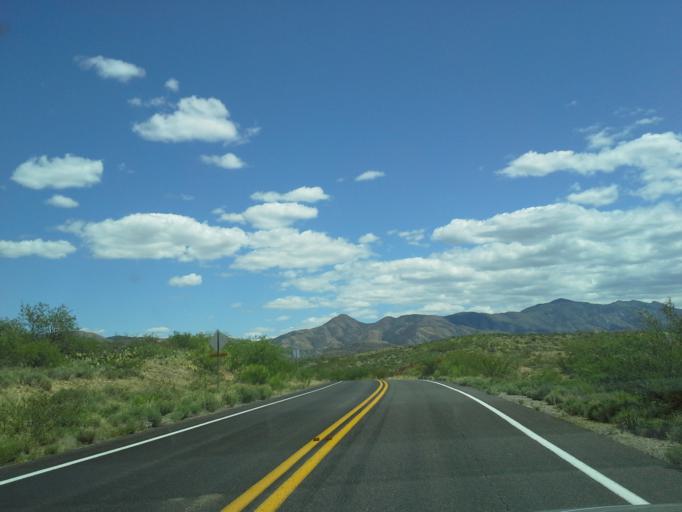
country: US
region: Arizona
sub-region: Pinal County
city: Oracle
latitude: 32.5910
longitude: -110.8468
